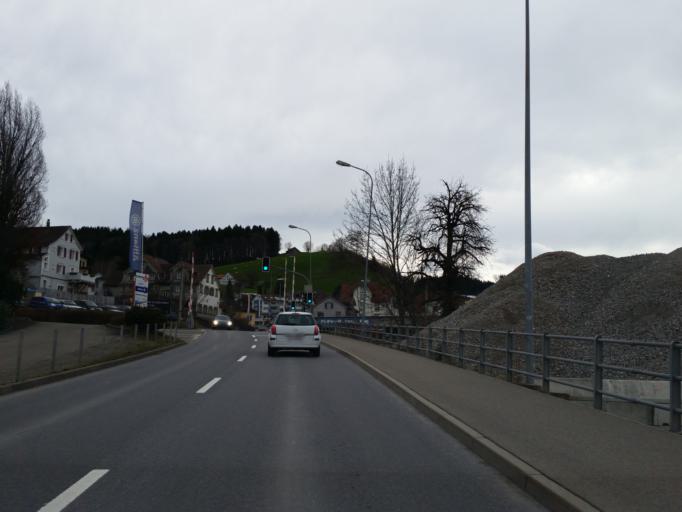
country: CH
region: Appenzell Ausserrhoden
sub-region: Bezirk Hinterland
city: Herisau
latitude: 47.3813
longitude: 9.2769
